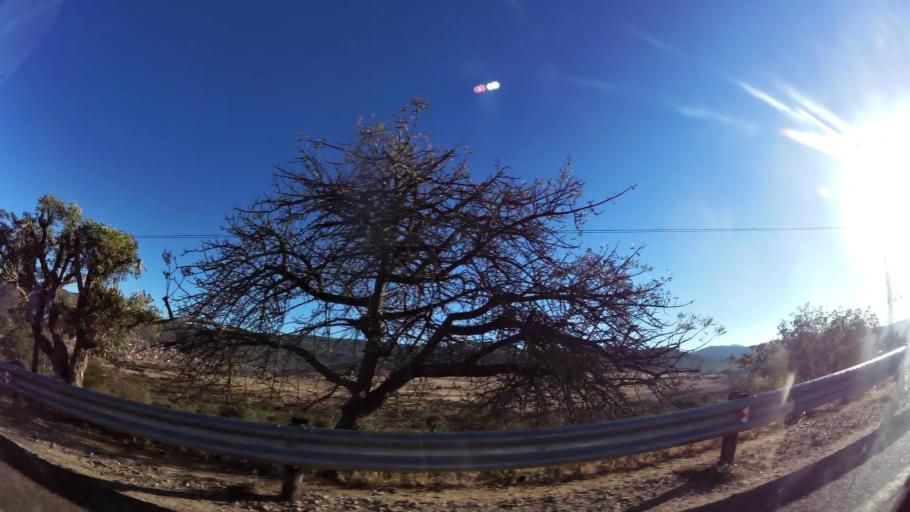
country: ZA
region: Limpopo
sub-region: Capricorn District Municipality
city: Mankoeng
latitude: -23.9197
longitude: 29.8808
